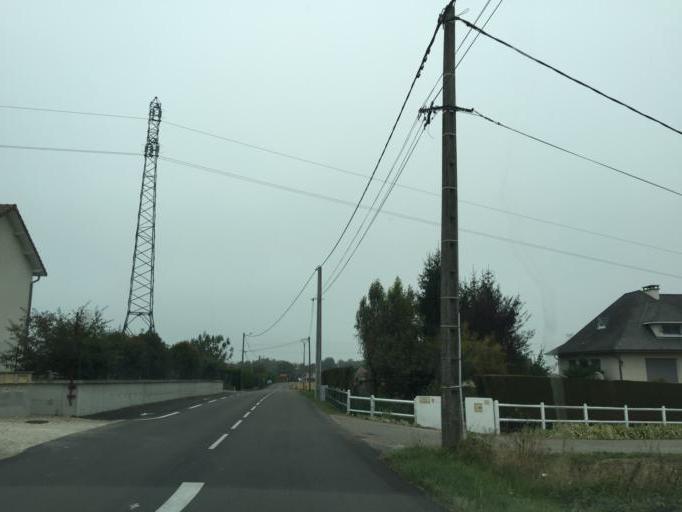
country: FR
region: Rhone-Alpes
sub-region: Departement de l'Isere
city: Faverges-de-la-Tour
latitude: 45.5855
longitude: 5.5096
